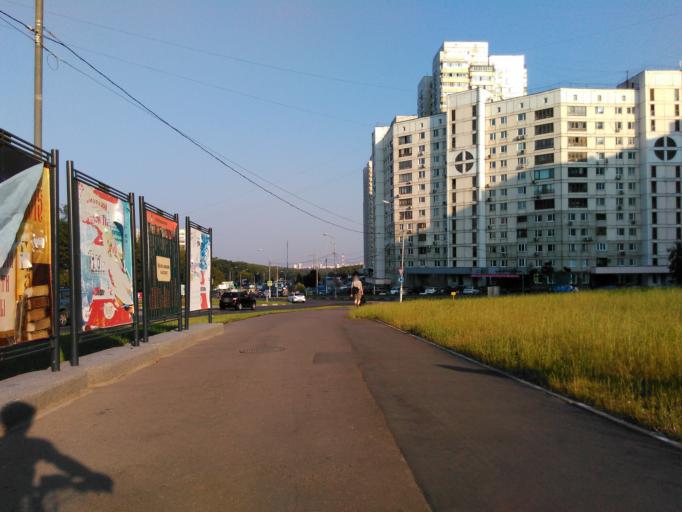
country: RU
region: Moskovskaya
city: Cheremushki
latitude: 55.6395
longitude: 37.5371
